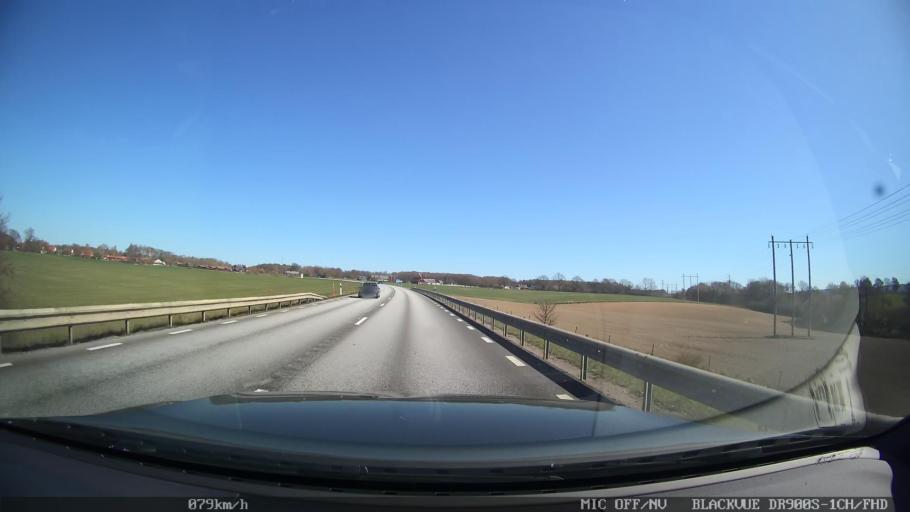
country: SE
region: Skane
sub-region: Klippans Kommun
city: Klippan
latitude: 56.1170
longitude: 13.1448
